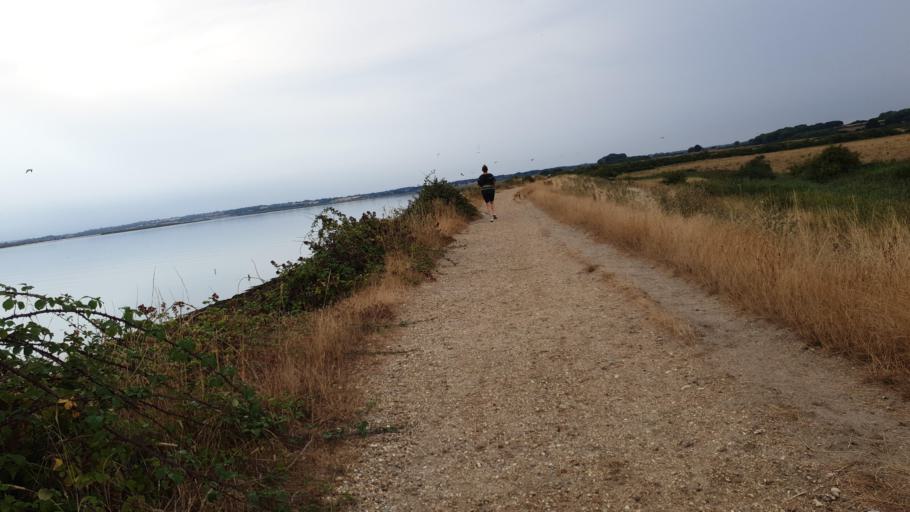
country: GB
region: England
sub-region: Essex
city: Brightlingsea
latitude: 51.8086
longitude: 1.0064
